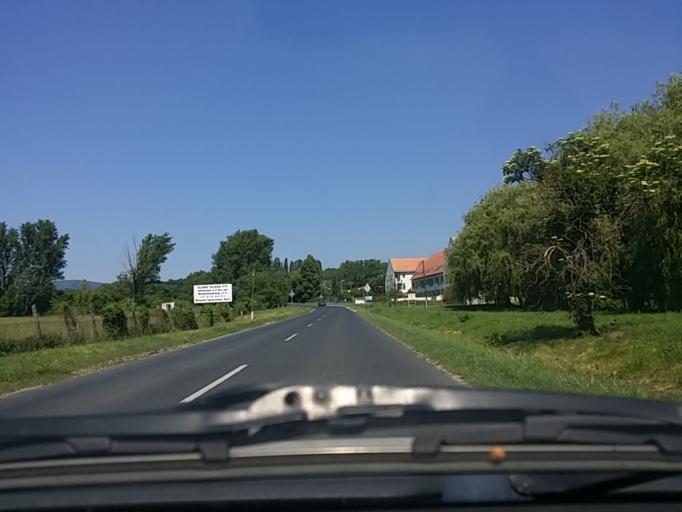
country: HU
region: Pest
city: Csobanka
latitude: 47.6618
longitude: 18.9727
